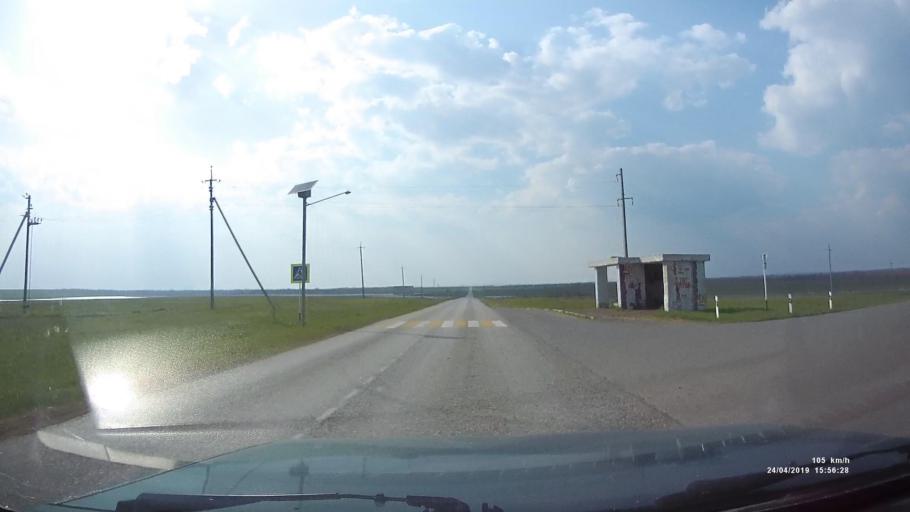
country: RU
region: Kalmykiya
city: Yashalta
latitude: 46.5980
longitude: 42.5281
